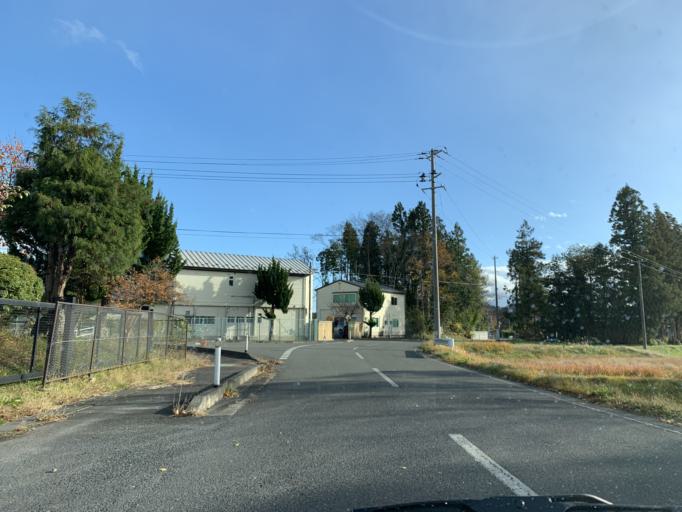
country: JP
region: Iwate
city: Mizusawa
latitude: 39.0265
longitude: 141.0773
